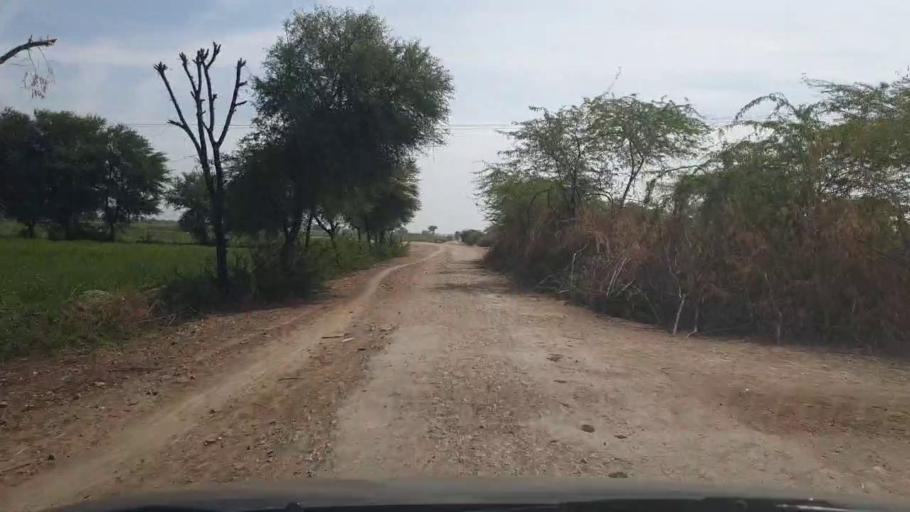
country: PK
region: Sindh
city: Umarkot
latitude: 25.3304
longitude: 69.6145
